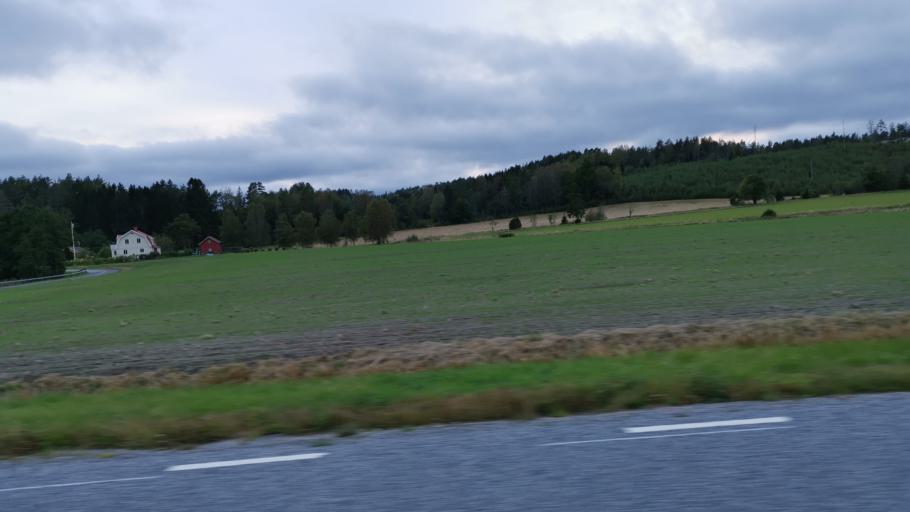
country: SE
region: Vaestra Goetaland
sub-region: Tanums Kommun
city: Tanumshede
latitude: 58.6796
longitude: 11.3388
